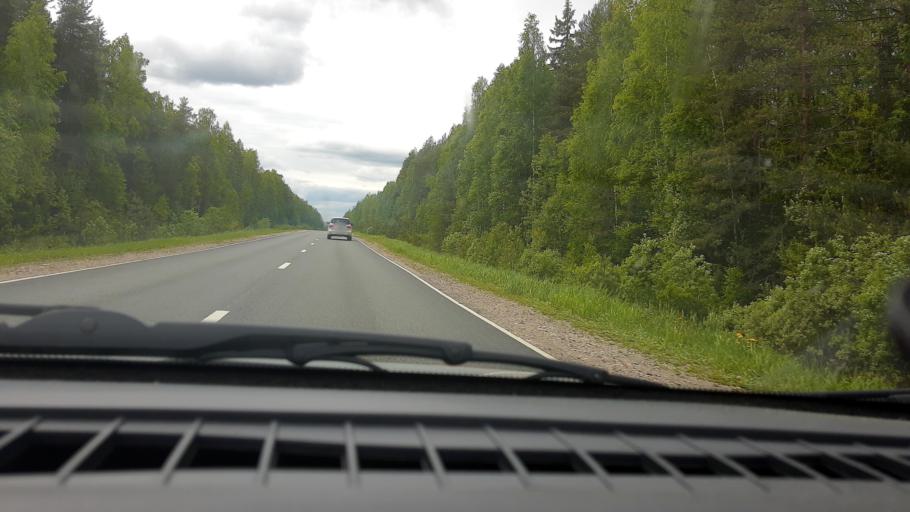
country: RU
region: Nizjnij Novgorod
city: Krasnyye Baki
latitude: 57.1493
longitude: 45.2578
